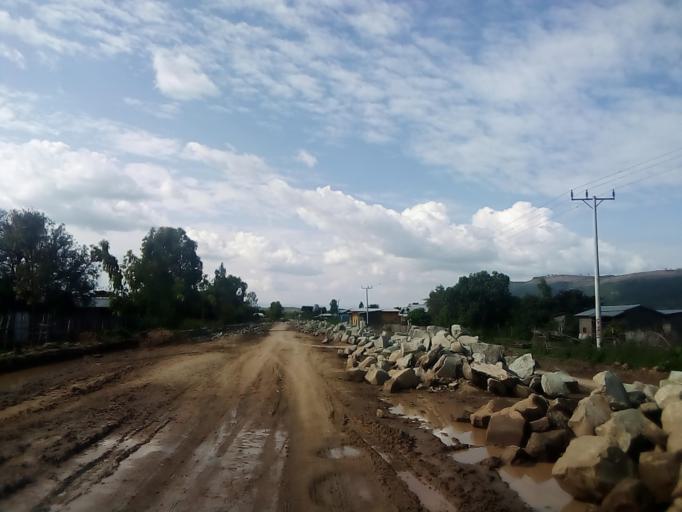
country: ET
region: Southern Nations, Nationalities, and People's Region
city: K'olito
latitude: 7.6037
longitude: 38.0666
